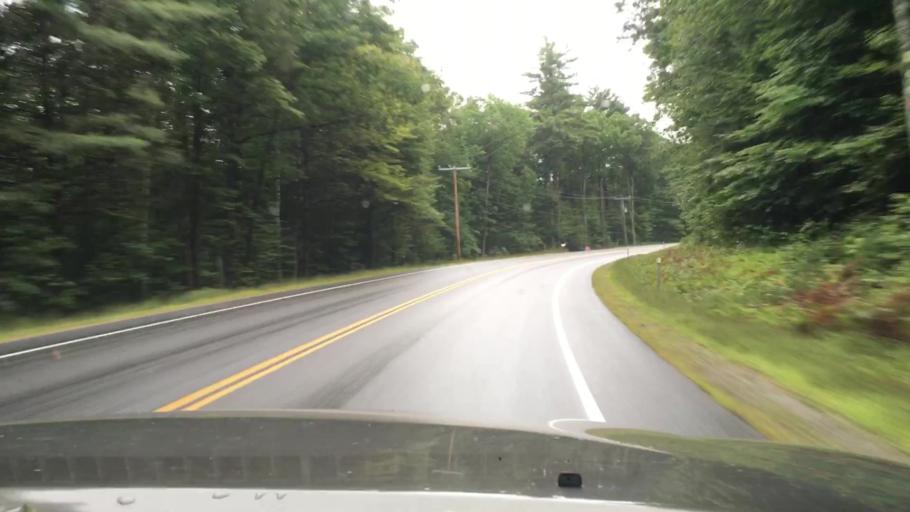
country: US
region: New Hampshire
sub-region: Hillsborough County
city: Antrim
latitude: 43.0858
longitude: -71.9653
